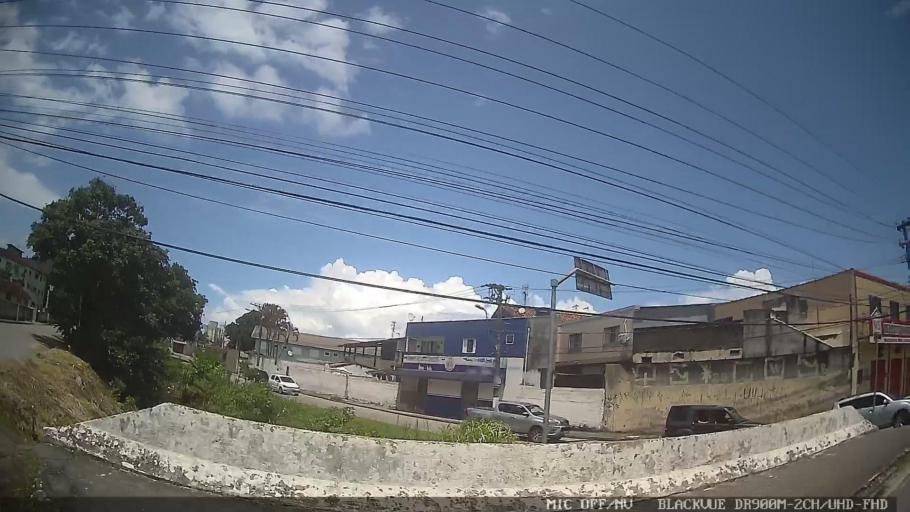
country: BR
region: Sao Paulo
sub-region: Caraguatatuba
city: Caraguatatuba
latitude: -23.6153
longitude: -45.3873
